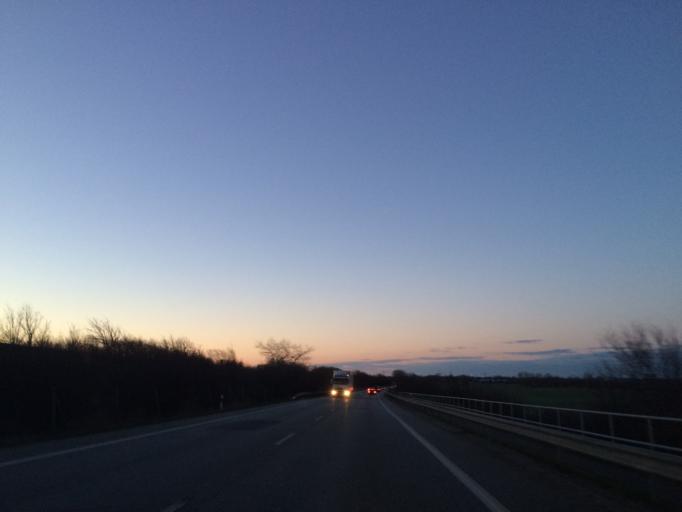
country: DE
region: Schleswig-Holstein
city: Grossenbrode
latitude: 54.3926
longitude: 11.1064
